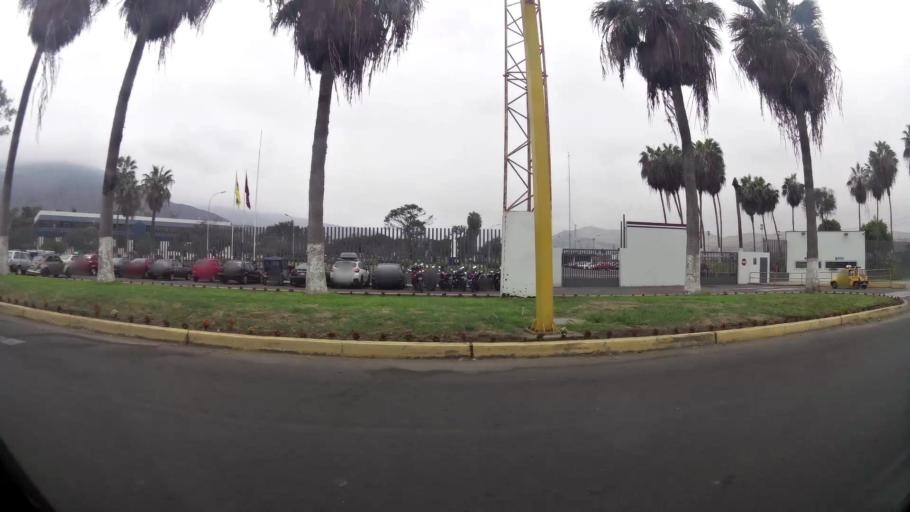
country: PE
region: Ancash
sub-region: Provincia de Santa
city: Chimbote
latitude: -9.0666
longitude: -78.5977
